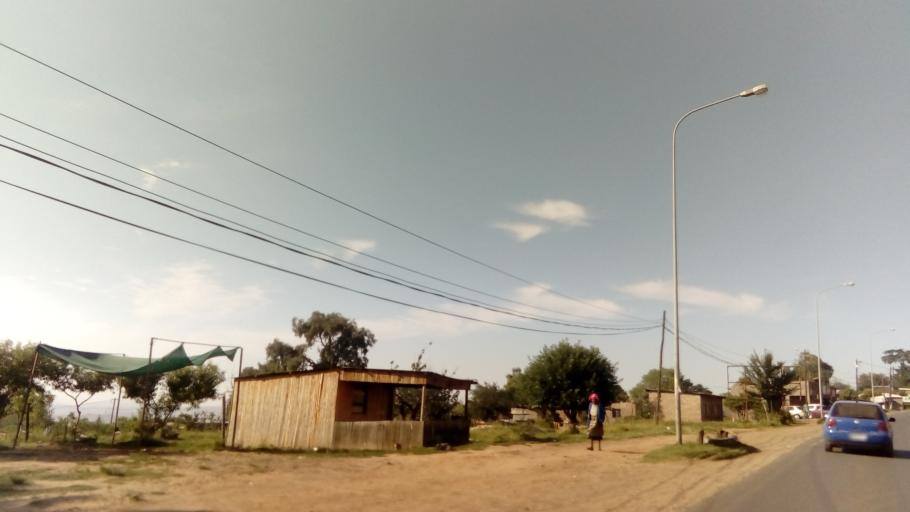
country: LS
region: Berea
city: Teyateyaneng
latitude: -29.1515
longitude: 27.7459
